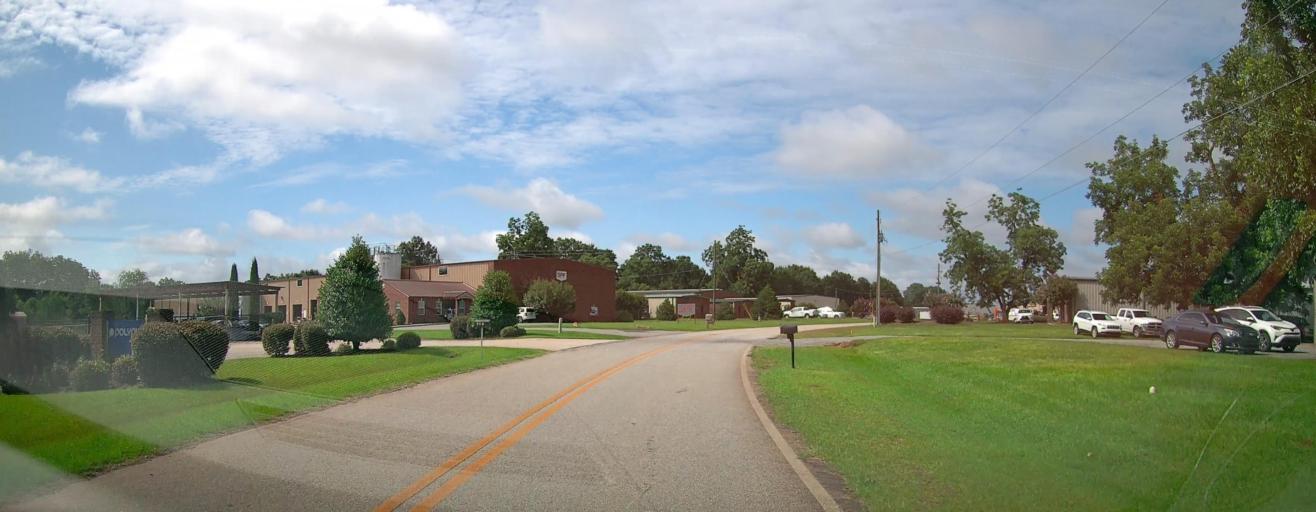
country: US
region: Georgia
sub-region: Peach County
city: Byron
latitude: 32.6485
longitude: -83.7365
